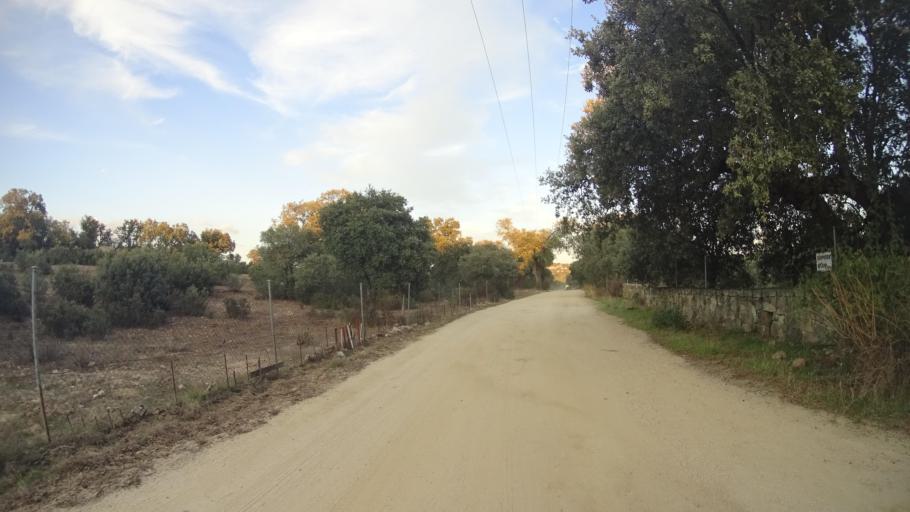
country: ES
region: Madrid
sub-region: Provincia de Madrid
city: Colmenarejo
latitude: 40.5565
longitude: -4.0314
